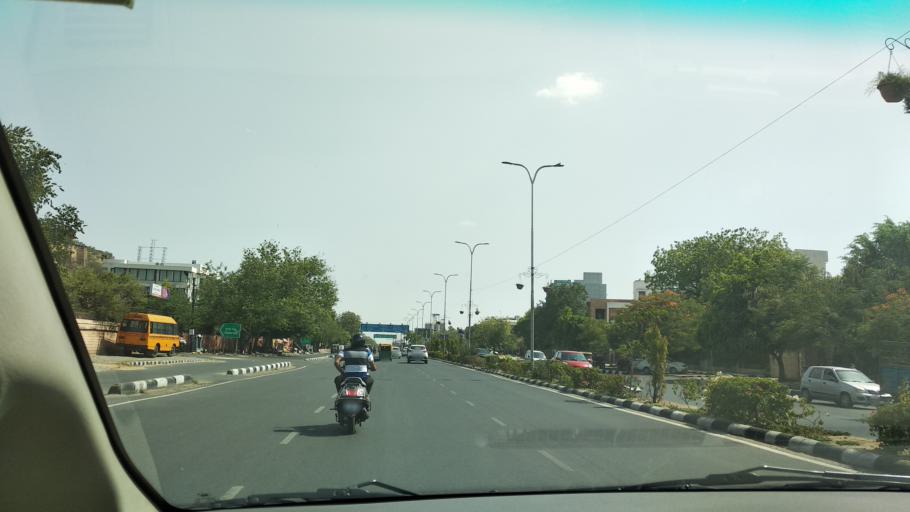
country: IN
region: Rajasthan
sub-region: Jaipur
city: Jaipur
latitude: 26.8973
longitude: 75.8159
